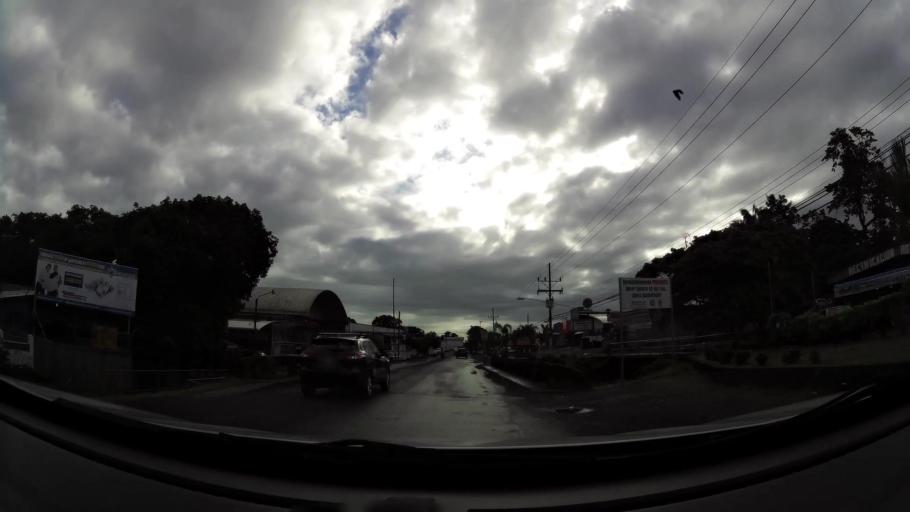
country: CR
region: Limon
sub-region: Canton de Pococi
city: Guapiles
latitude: 10.2133
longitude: -83.7866
